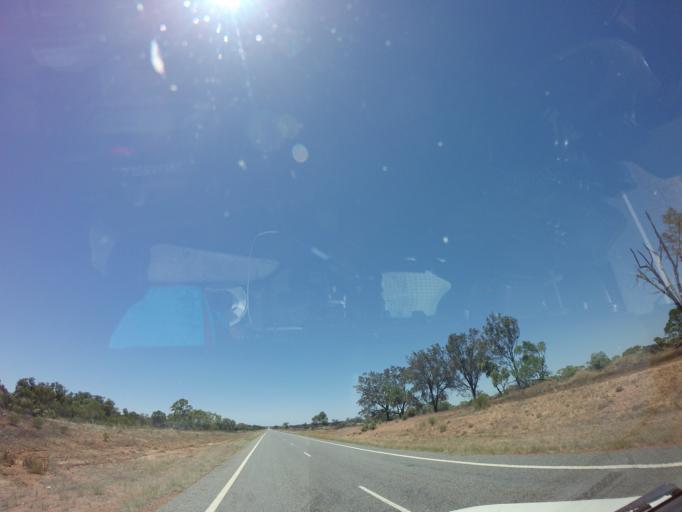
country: AU
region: New South Wales
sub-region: Cobar
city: Cobar
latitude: -31.5802
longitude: 144.8172
